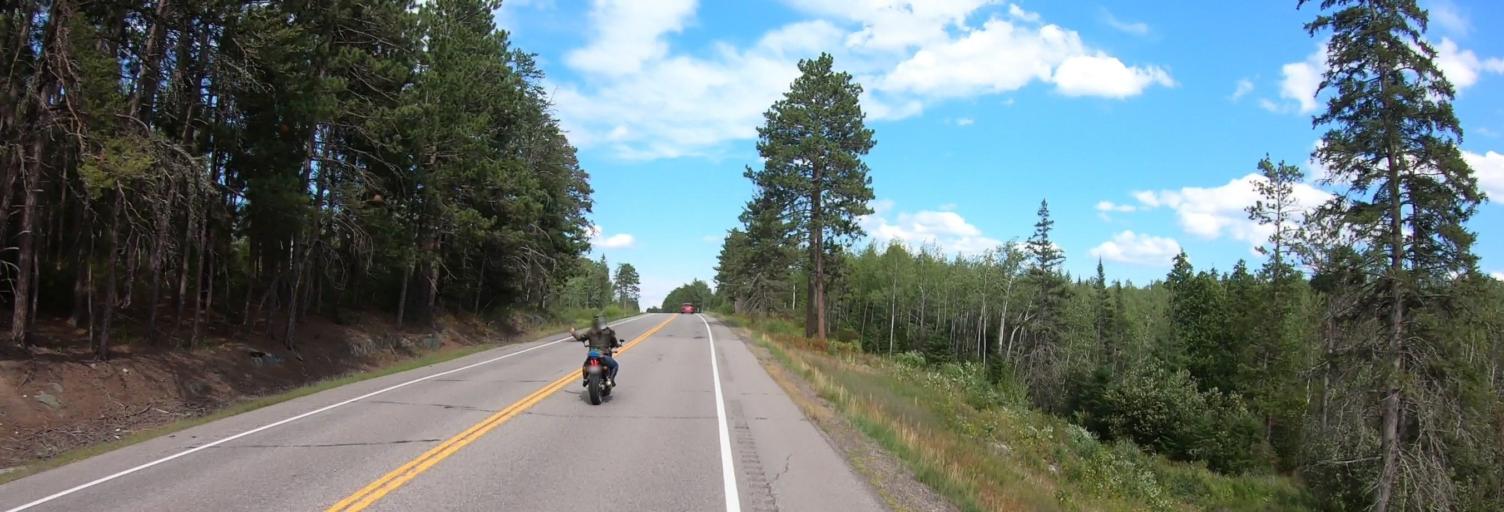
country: US
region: Minnesota
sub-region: Saint Louis County
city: Babbitt
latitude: 47.8179
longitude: -92.2061
